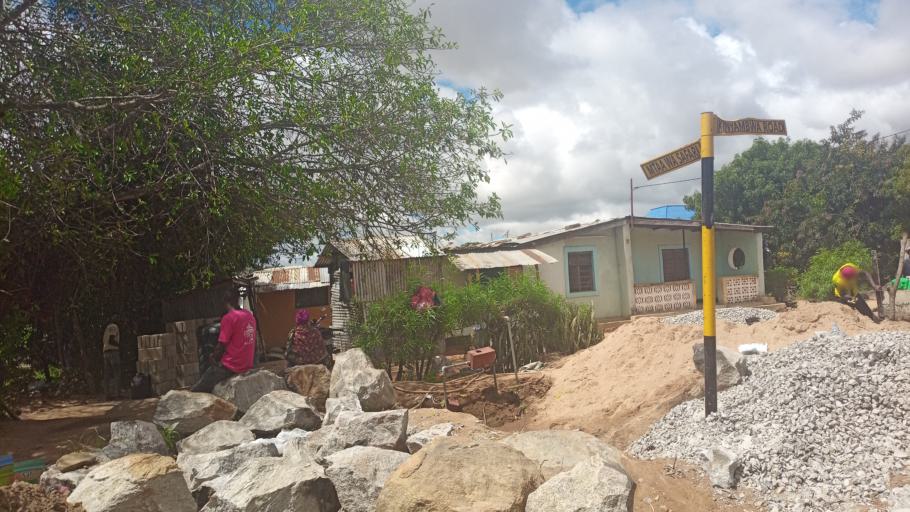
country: TZ
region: Dodoma
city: Dodoma
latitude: -6.1856
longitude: 35.7303
